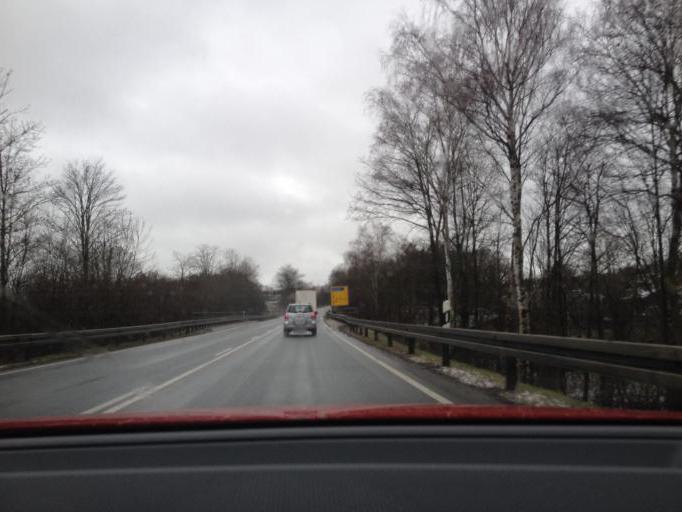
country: DE
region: Bavaria
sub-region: Upper Franconia
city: Dohlau
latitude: 50.2852
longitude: 11.9331
